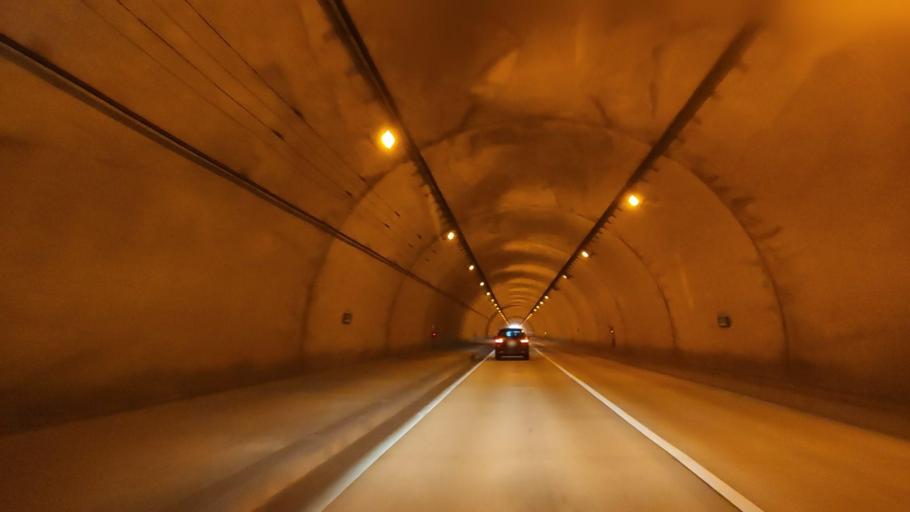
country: JP
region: Ehime
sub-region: Shikoku-chuo Shi
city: Matsuyama
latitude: 33.8834
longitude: 132.7095
